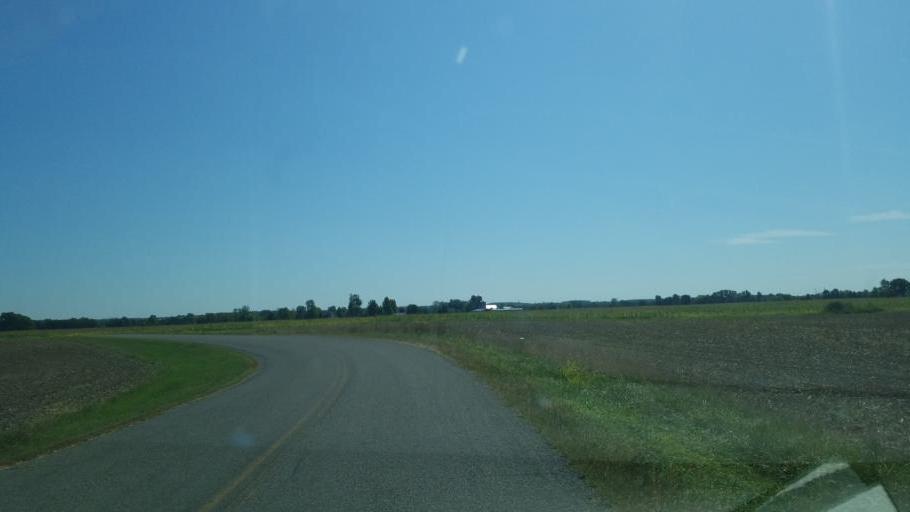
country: US
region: Ohio
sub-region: Logan County
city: Northwood
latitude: 40.5174
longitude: -83.7658
